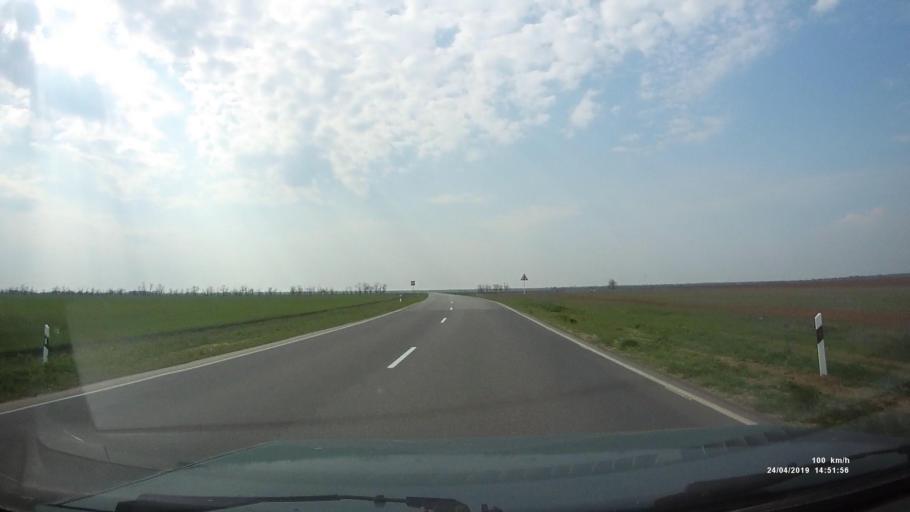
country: RU
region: Rostov
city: Remontnoye
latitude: 46.5288
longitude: 43.6905
